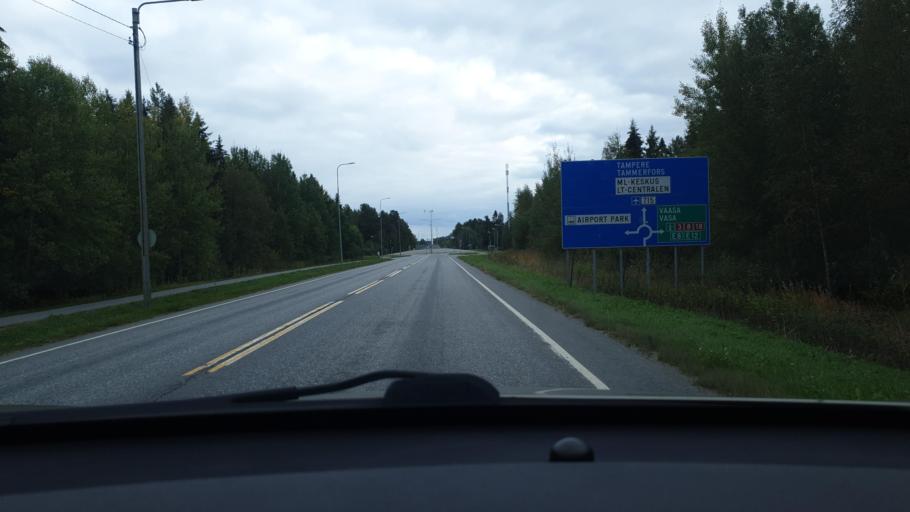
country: FI
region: Ostrobothnia
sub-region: Vaasa
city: Ristinummi
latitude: 63.0561
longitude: 21.7169
